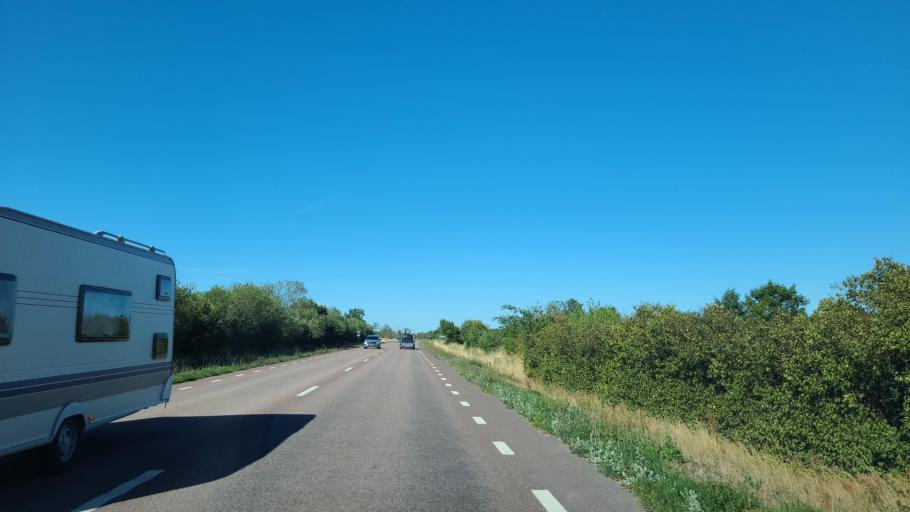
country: SE
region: Kalmar
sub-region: Borgholms Kommun
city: Borgholm
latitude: 57.0274
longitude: 16.8614
